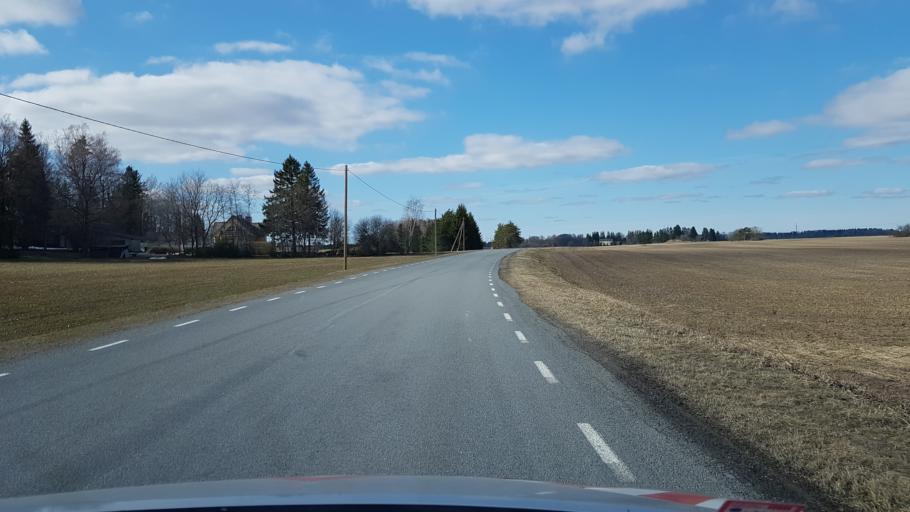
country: EE
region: Laeaene-Virumaa
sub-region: Tamsalu vald
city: Tamsalu
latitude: 59.1691
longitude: 26.0624
